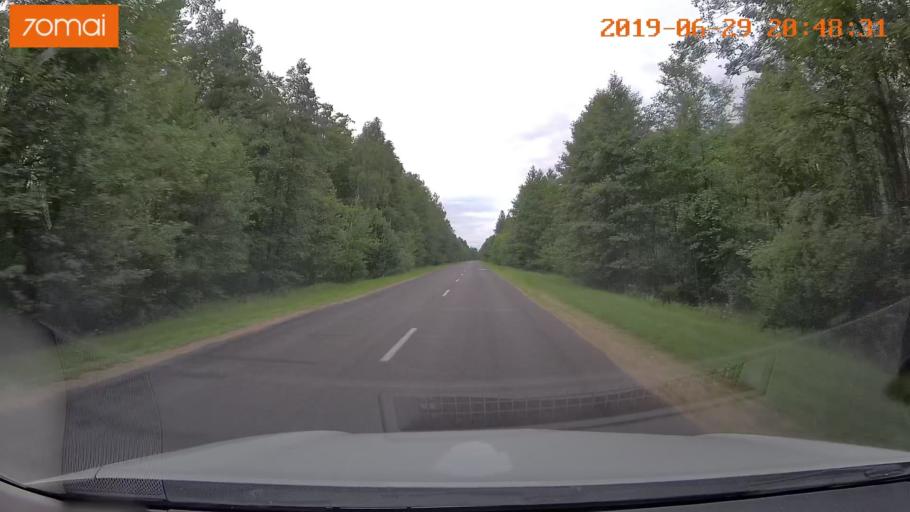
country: BY
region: Brest
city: Hantsavichy
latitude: 52.6520
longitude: 26.3179
